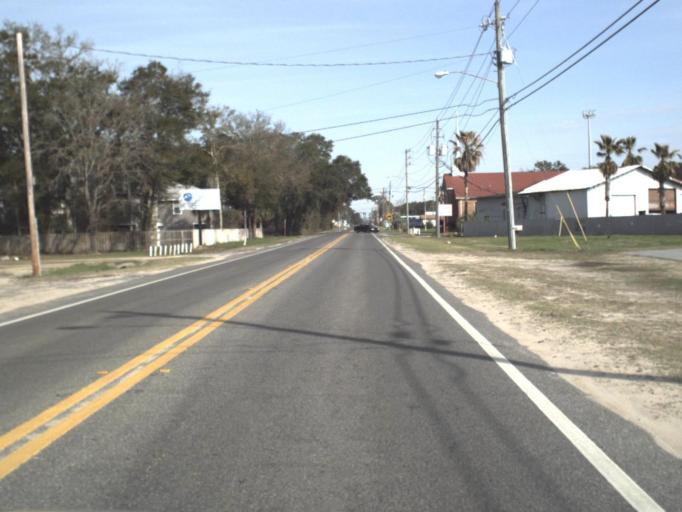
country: US
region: Florida
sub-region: Bay County
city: Parker
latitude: 30.1311
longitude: -85.6095
